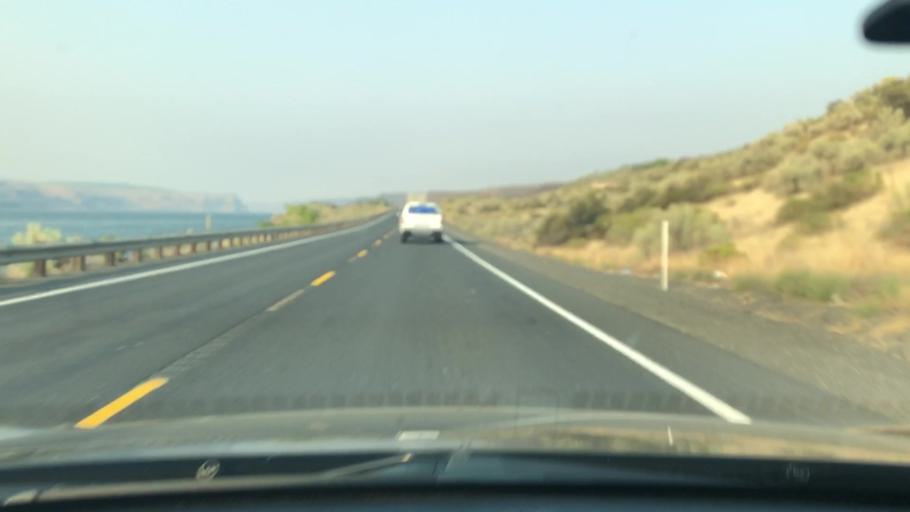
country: US
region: Oregon
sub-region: Umatilla County
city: Stanfield
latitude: 45.9245
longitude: -119.1108
